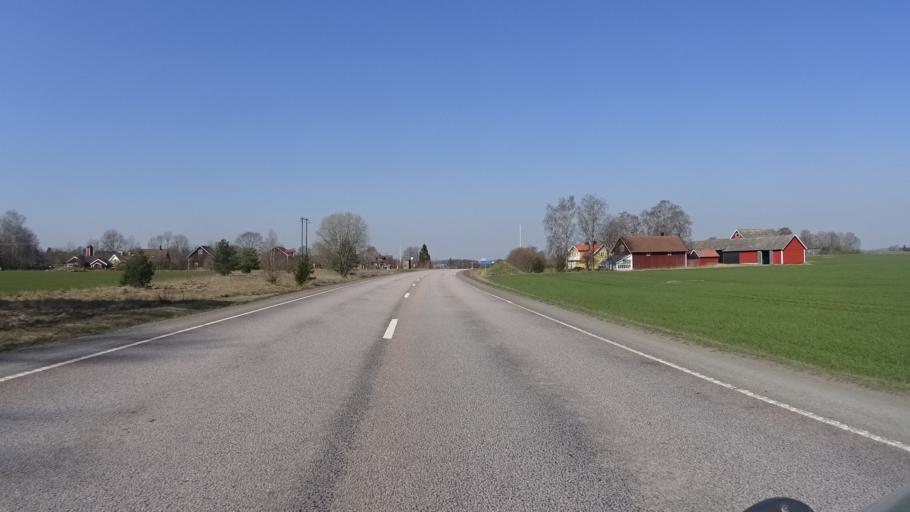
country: SE
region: OEstergoetland
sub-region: Mjolby Kommun
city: Mantorp
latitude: 58.3776
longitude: 15.1996
